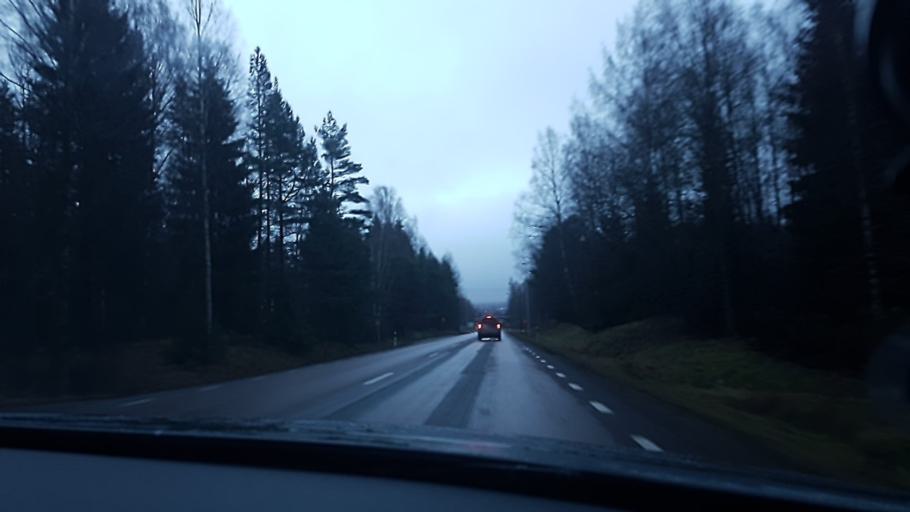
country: SE
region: Vaermland
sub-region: Kristinehamns Kommun
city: Kristinehamn
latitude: 59.3285
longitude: 14.1173
